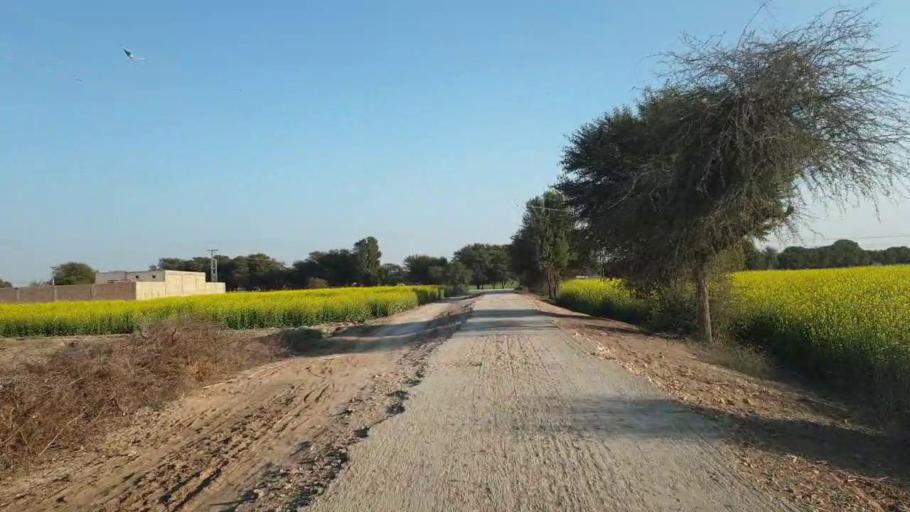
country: PK
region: Sindh
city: Shahpur Chakar
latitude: 26.1262
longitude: 68.5594
